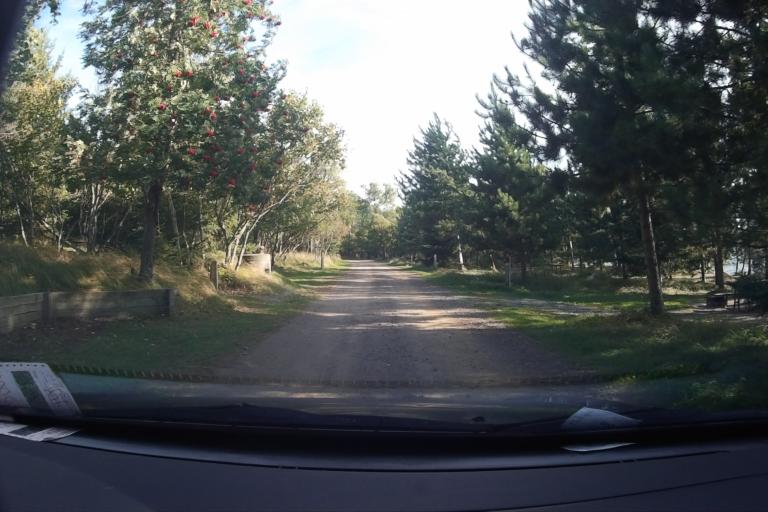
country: CA
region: Ontario
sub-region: Thunder Bay District
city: Thunder Bay
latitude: 48.3711
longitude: -88.8070
